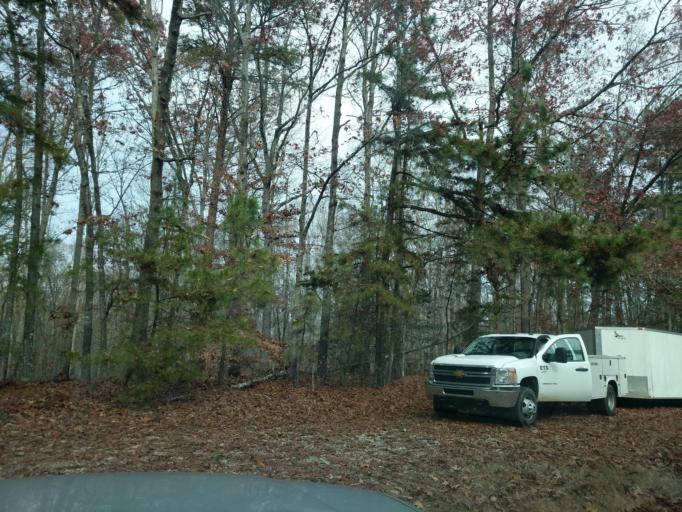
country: US
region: South Carolina
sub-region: Anderson County
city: Pendleton
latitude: 34.6532
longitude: -82.8127
